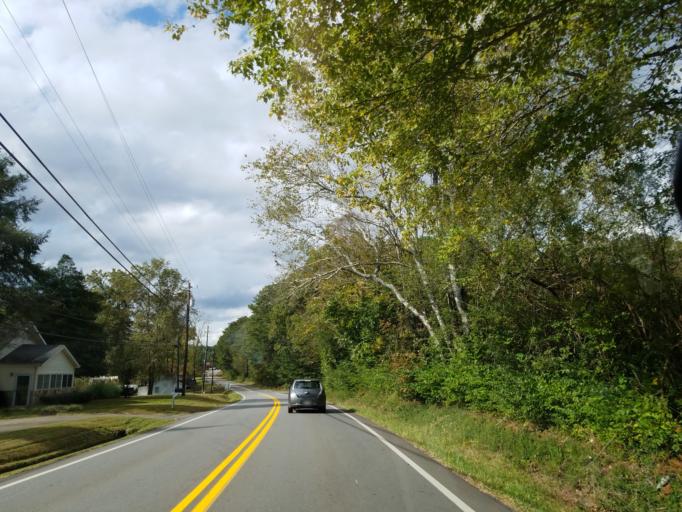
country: US
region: Georgia
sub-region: Pickens County
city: Jasper
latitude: 34.4536
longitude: -84.4250
